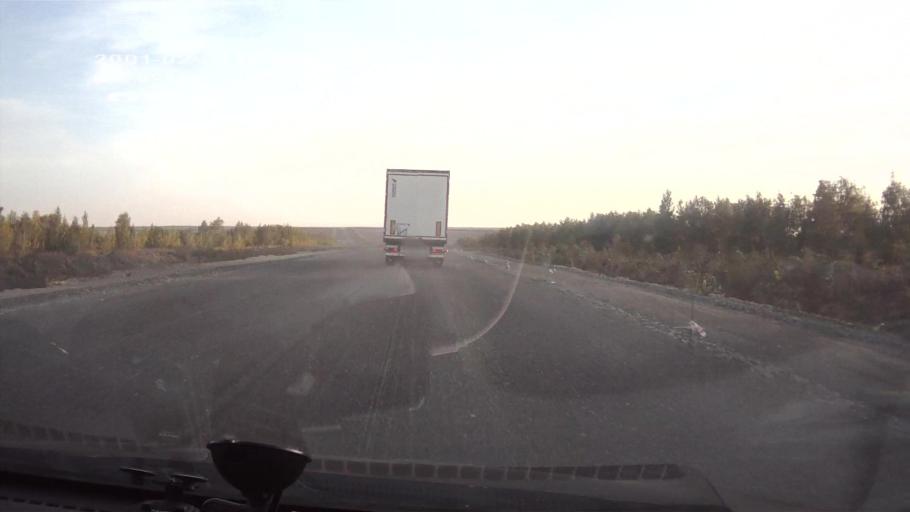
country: RU
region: Saratov
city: Krasnoarmeysk
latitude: 50.9985
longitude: 45.6133
